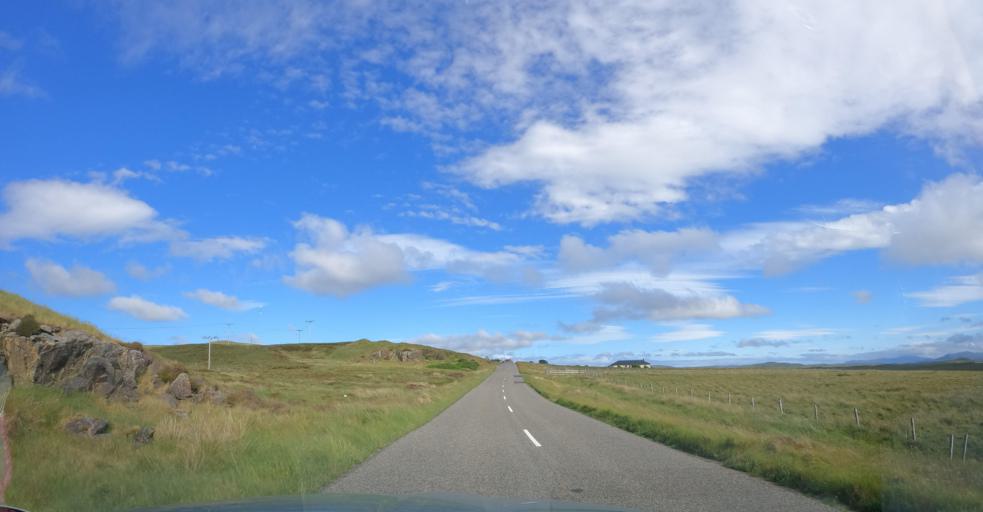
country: GB
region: Scotland
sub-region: Eilean Siar
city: Stornoway
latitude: 58.1763
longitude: -6.6172
